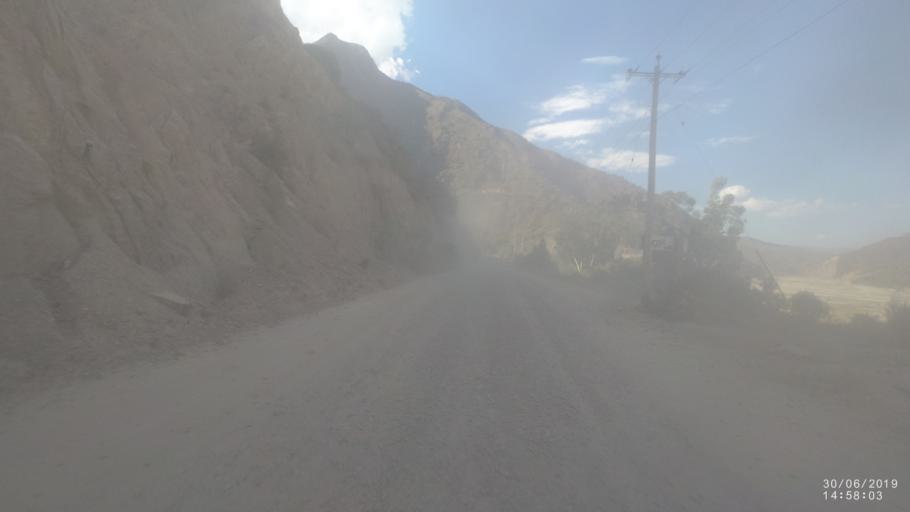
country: BO
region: Cochabamba
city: Irpa Irpa
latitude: -17.7408
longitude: -66.3512
